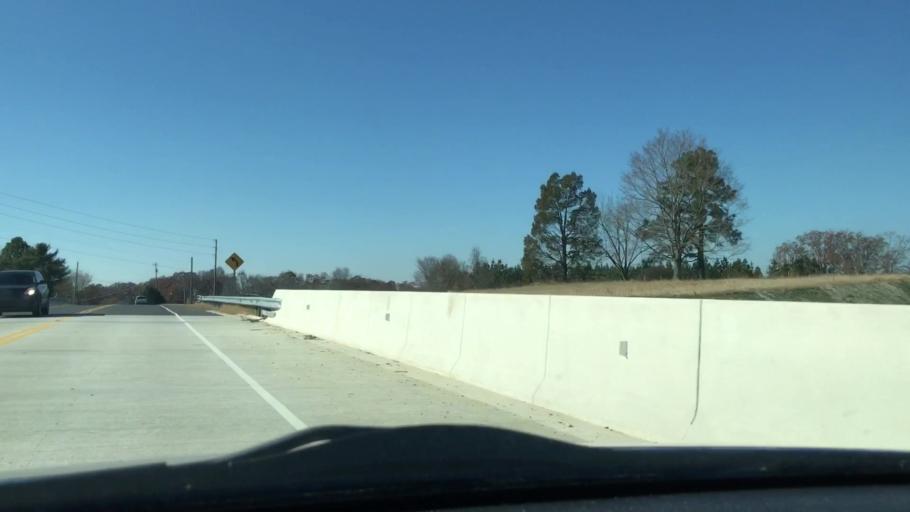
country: US
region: North Carolina
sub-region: Randolph County
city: Asheboro
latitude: 35.6817
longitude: -79.8648
